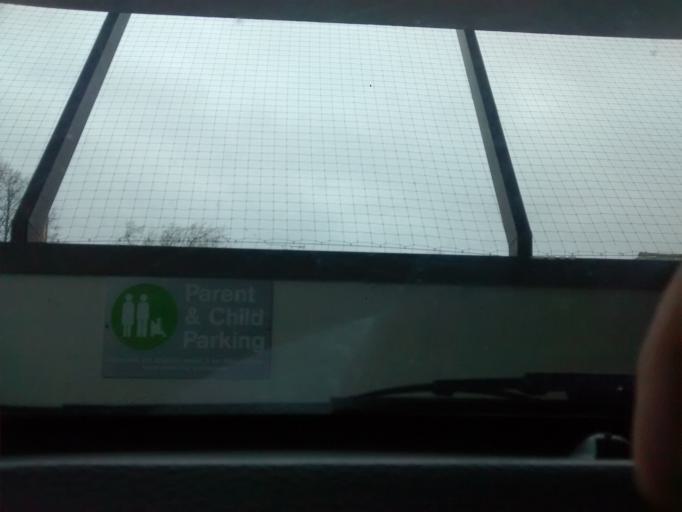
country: GB
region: England
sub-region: Cambridgeshire
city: Cambridge
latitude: 52.2072
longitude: 0.1340
